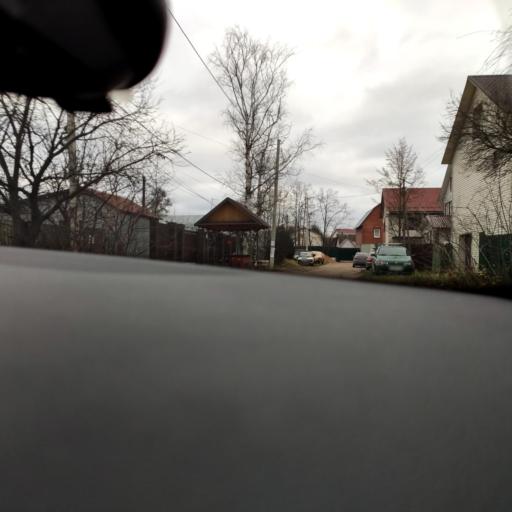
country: RU
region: Moskovskaya
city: Lobnya
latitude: 56.0084
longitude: 37.5046
